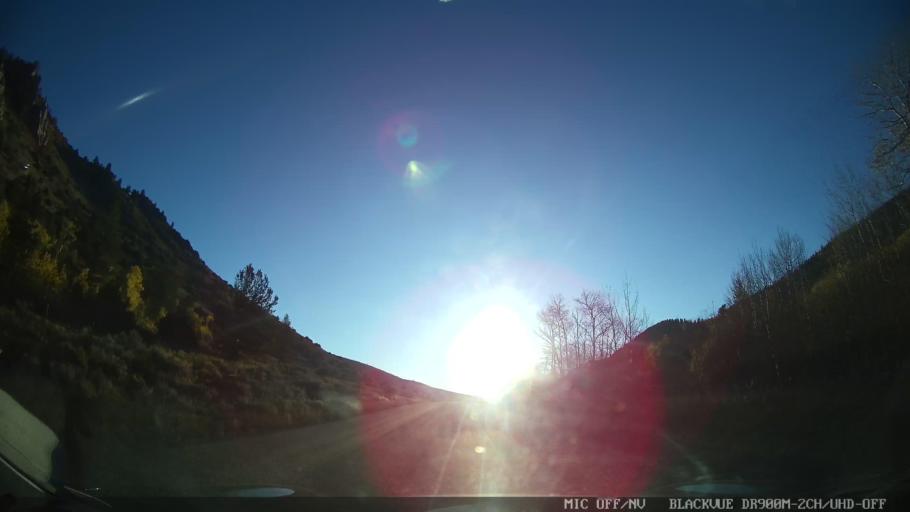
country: US
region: Colorado
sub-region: Grand County
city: Kremmling
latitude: 39.9937
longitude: -106.4700
